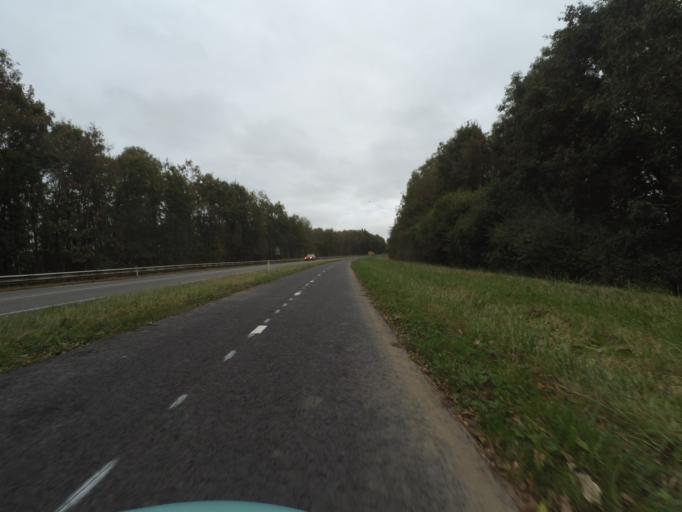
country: NL
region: Gelderland
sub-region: Gemeente Tiel
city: Tiel
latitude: 51.9206
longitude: 5.4235
